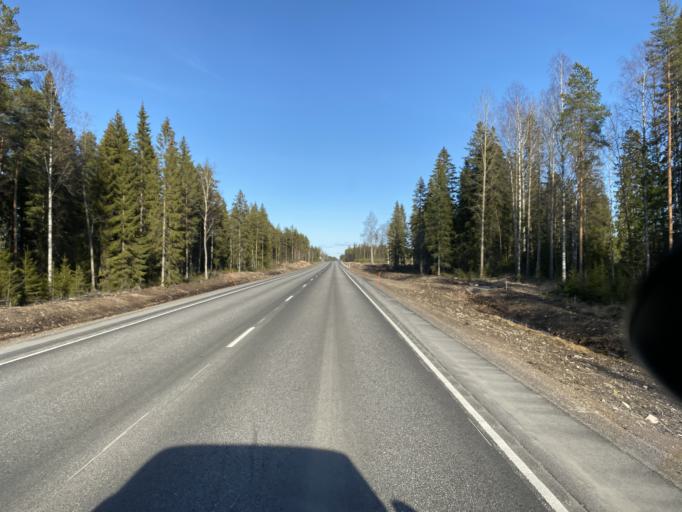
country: FI
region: Satakunta
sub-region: Pori
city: Kokemaeki
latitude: 61.1674
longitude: 22.4396
